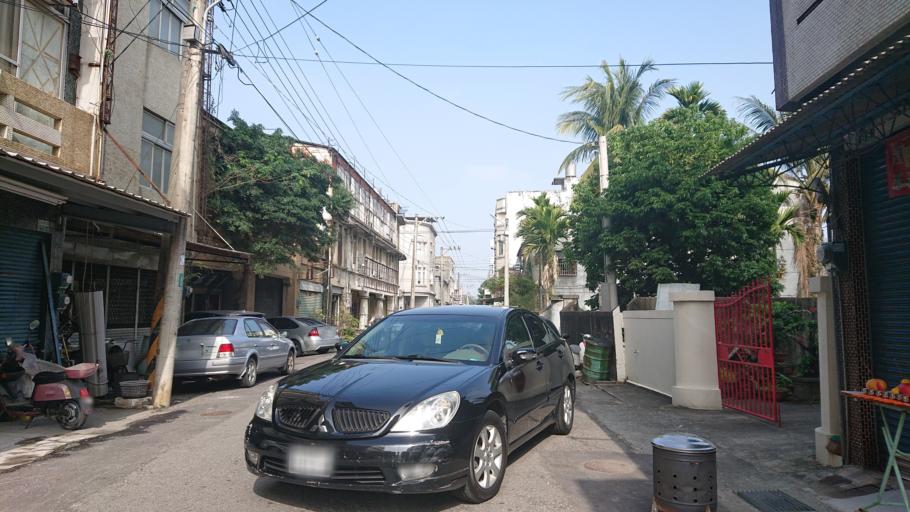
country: TW
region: Taiwan
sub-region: Chiayi
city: Taibao
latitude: 23.4679
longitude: 120.2441
